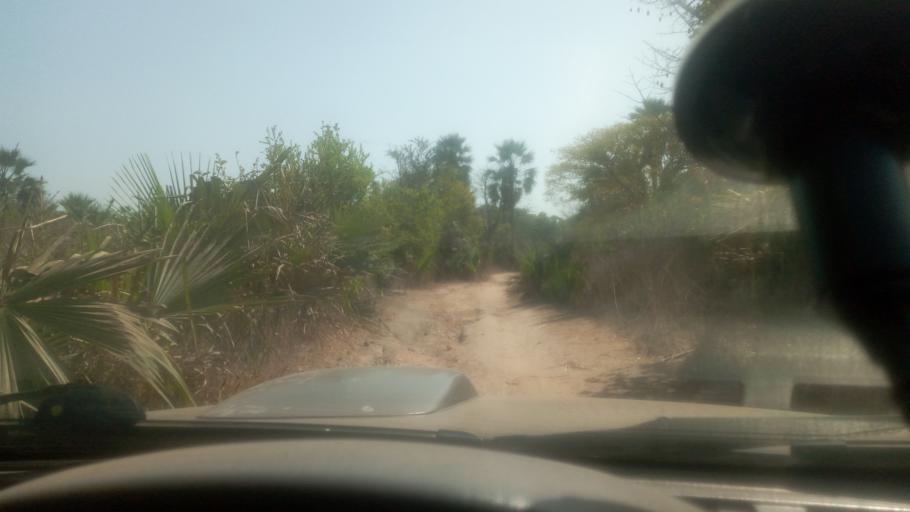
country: GW
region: Oio
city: Farim
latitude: 12.4581
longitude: -15.4077
